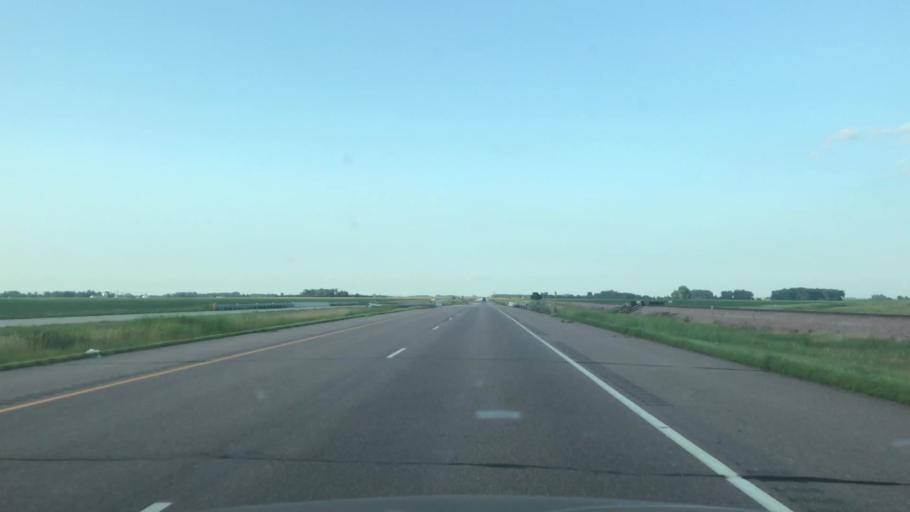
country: US
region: Minnesota
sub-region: Nobles County
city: Worthington
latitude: 43.7329
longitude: -95.4186
